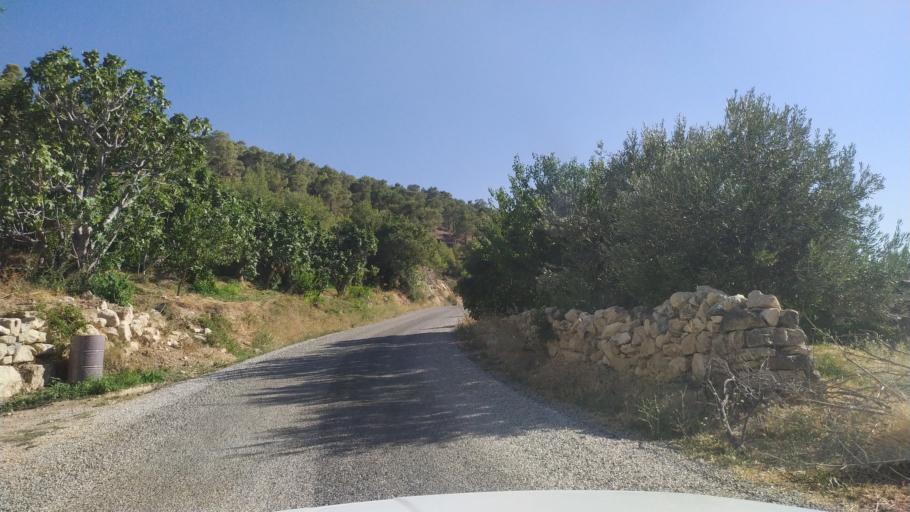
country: TR
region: Mersin
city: Mut
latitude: 36.7052
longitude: 33.4740
